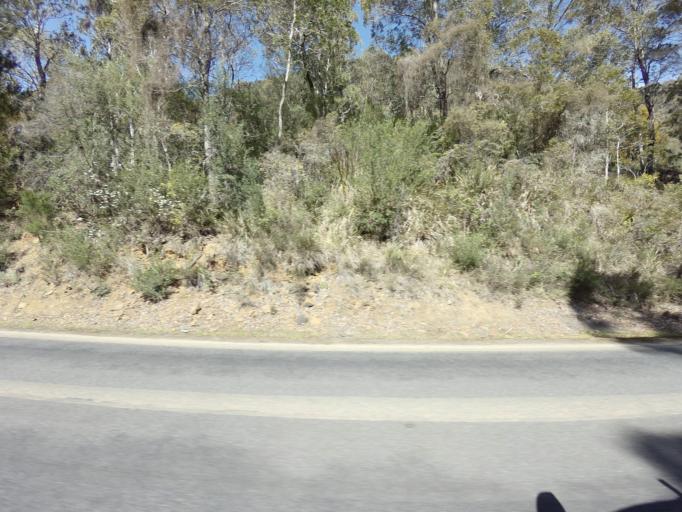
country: AU
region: Tasmania
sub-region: Derwent Valley
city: New Norfolk
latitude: -42.6774
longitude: 146.7565
